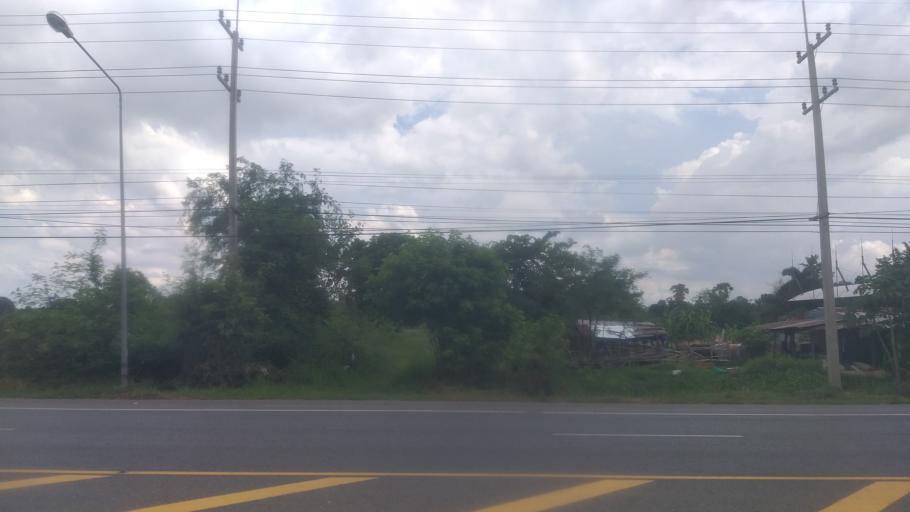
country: TH
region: Chaiyaphum
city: Noen Sa-nga
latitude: 15.6769
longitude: 101.9883
